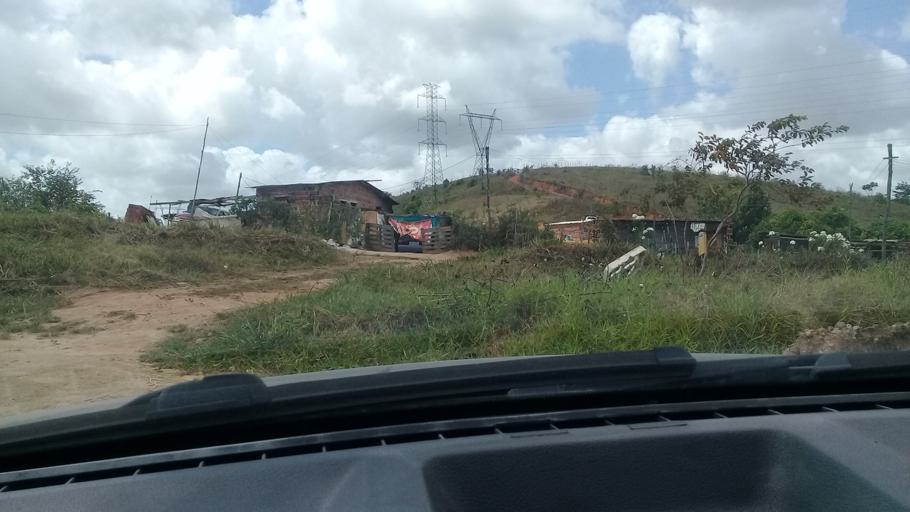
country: BR
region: Pernambuco
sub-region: Jaboatao Dos Guararapes
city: Jaboatao dos Guararapes
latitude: -8.0874
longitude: -35.0329
